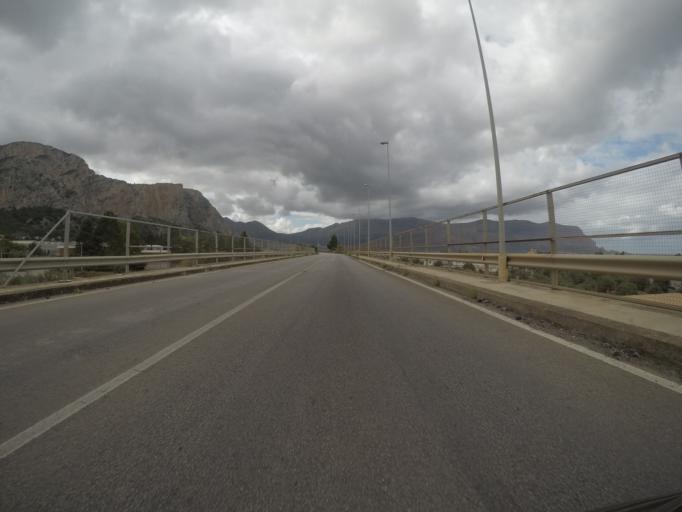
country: IT
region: Sicily
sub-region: Palermo
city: Capaci
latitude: 38.1653
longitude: 13.2208
